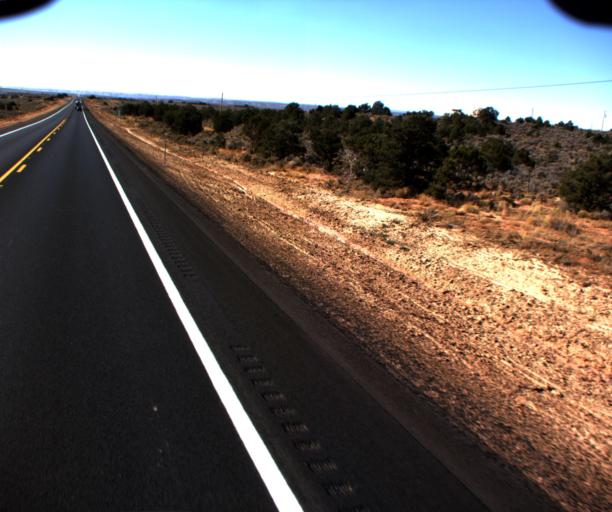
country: US
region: Arizona
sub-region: Apache County
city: Ganado
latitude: 35.7167
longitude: -109.4172
